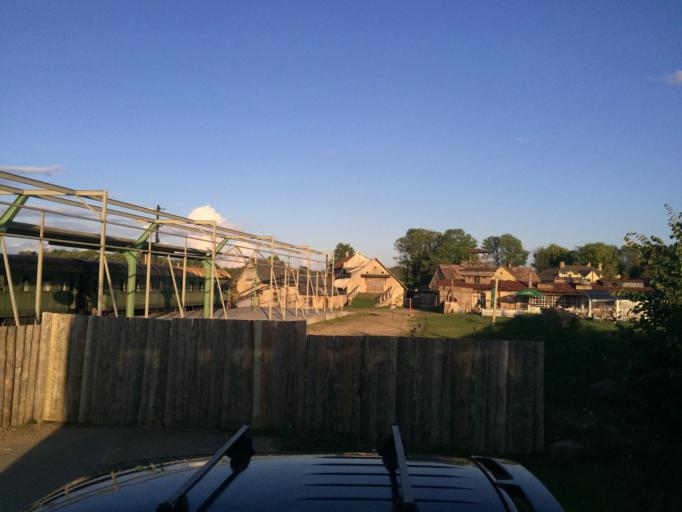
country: LV
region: Tukuma Rajons
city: Tukums
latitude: 56.8792
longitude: 23.2209
